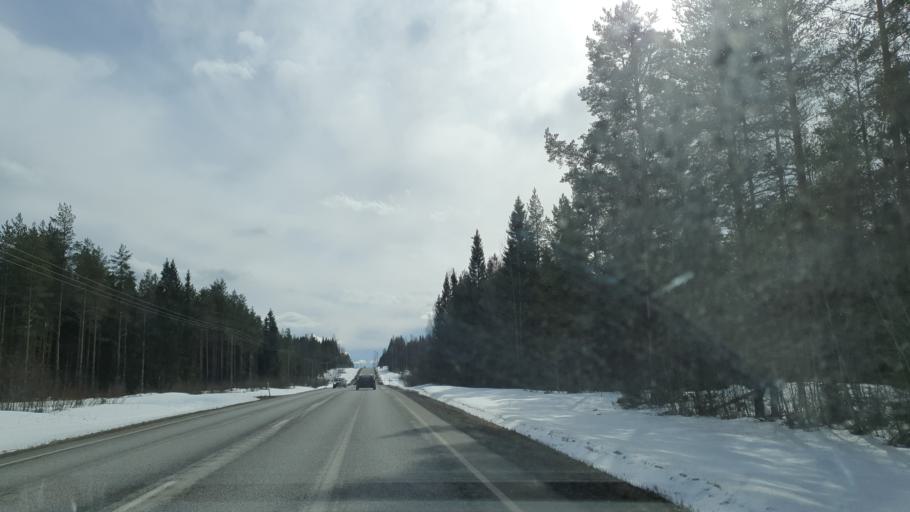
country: FI
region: Kainuu
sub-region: Kajaani
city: Ristijaervi
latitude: 64.3509
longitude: 28.0519
